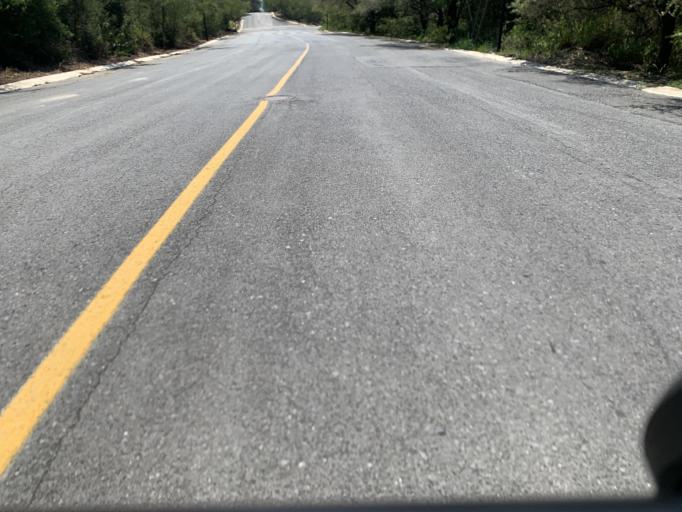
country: MX
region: Nuevo Leon
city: Santiago
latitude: 25.5097
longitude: -100.1806
